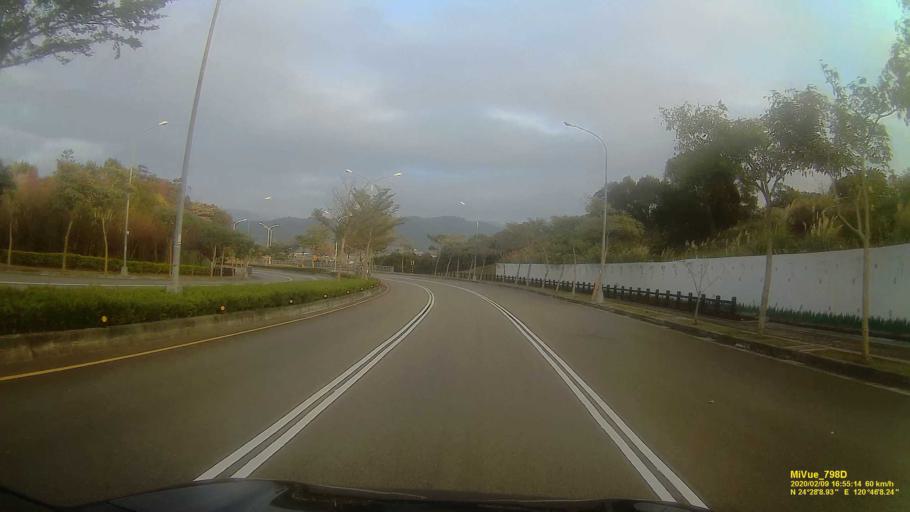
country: TW
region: Taiwan
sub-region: Miaoli
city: Miaoli
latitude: 24.4689
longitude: 120.7697
